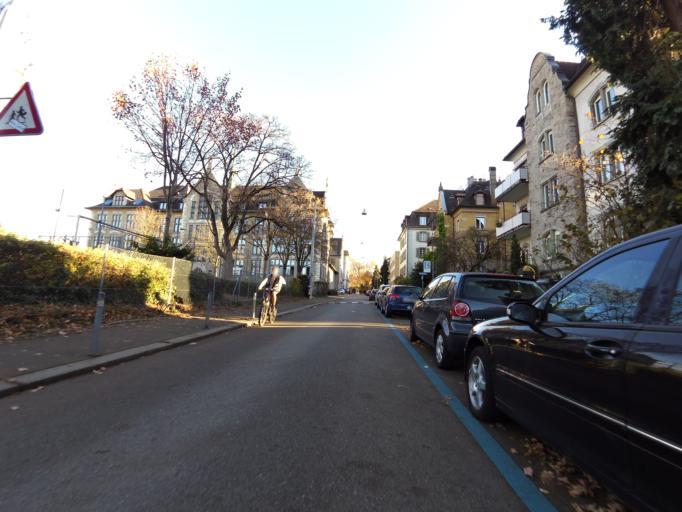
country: CH
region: Zurich
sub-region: Bezirk Zuerich
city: Zuerich (Kreis 3) / Sihlfeld
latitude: 47.3693
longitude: 8.5144
